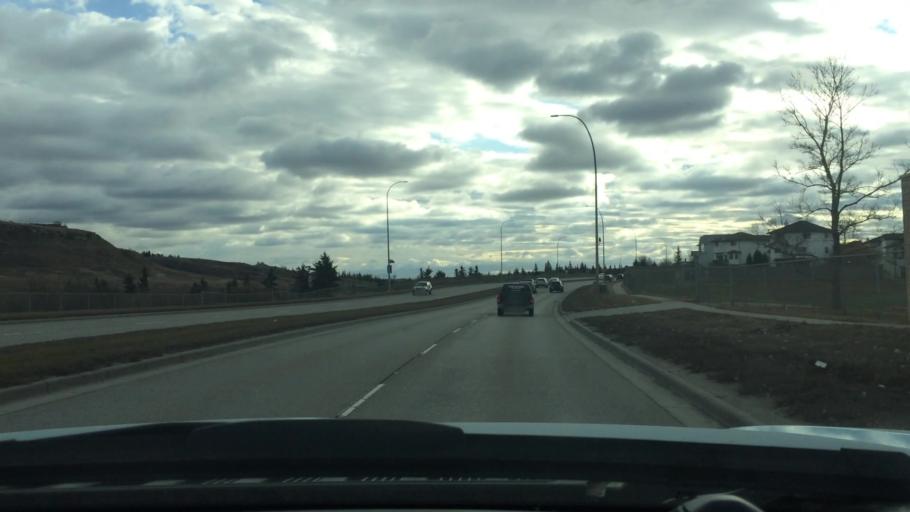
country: CA
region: Alberta
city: Calgary
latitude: 51.1515
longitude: -114.1008
